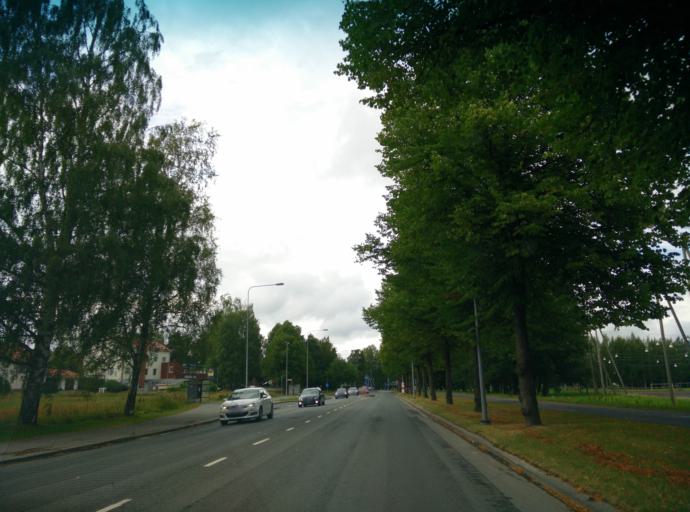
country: FI
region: Haeme
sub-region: Haemeenlinna
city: Haemeenlinna
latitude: 61.0016
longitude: 24.4281
